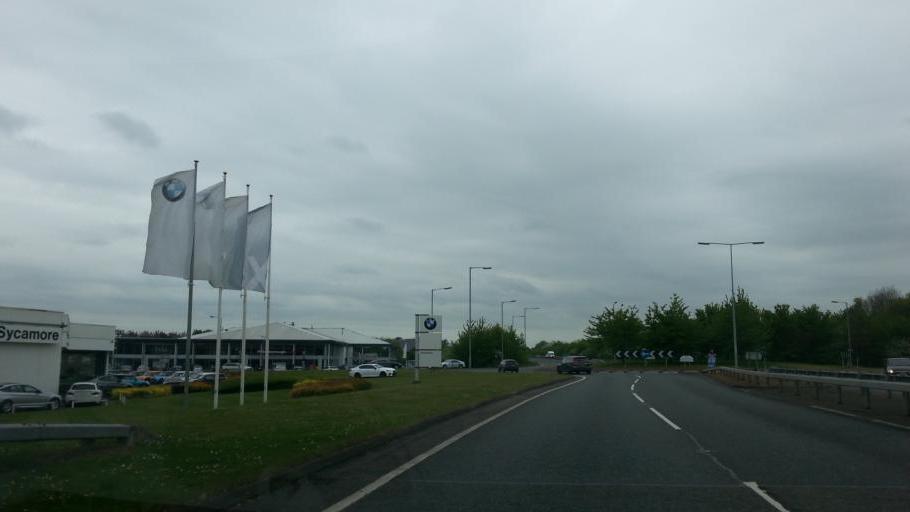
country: GB
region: England
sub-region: Peterborough
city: Glinton
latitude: 52.6180
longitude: -0.2881
